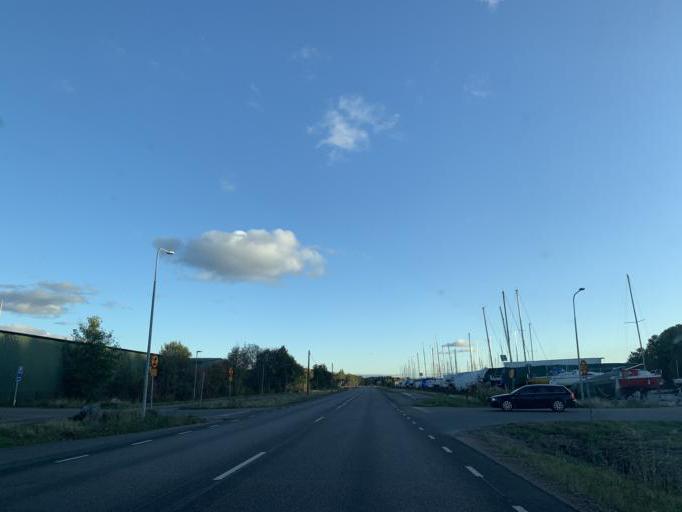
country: SE
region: Vaestmanland
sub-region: Vasteras
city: Vasteras
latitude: 59.5780
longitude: 16.5175
